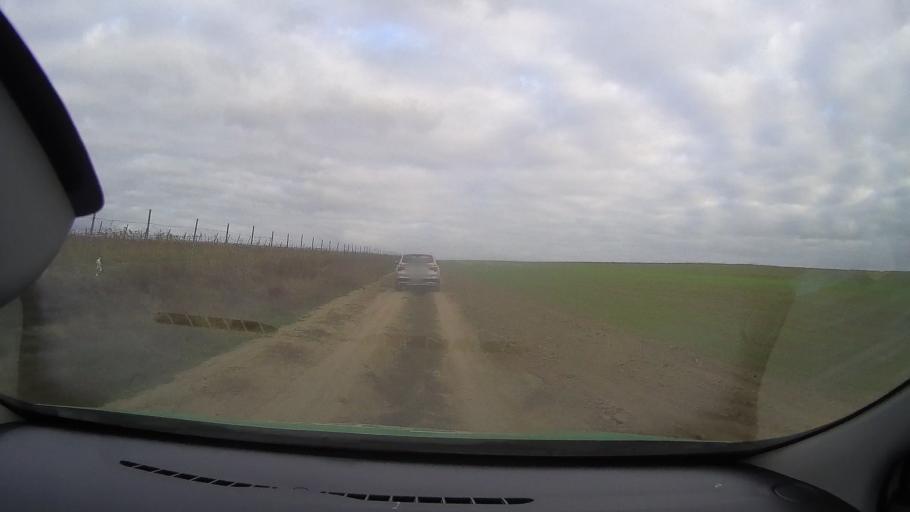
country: RO
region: Tulcea
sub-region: Comuna Jurilovca
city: Jurilovca
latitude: 44.7654
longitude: 28.9069
